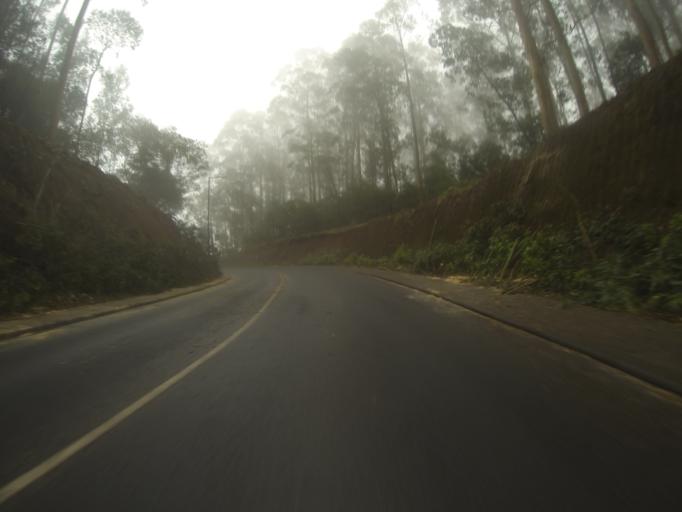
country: PT
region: Madeira
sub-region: Santa Cruz
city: Camacha
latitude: 32.6741
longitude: -16.8517
